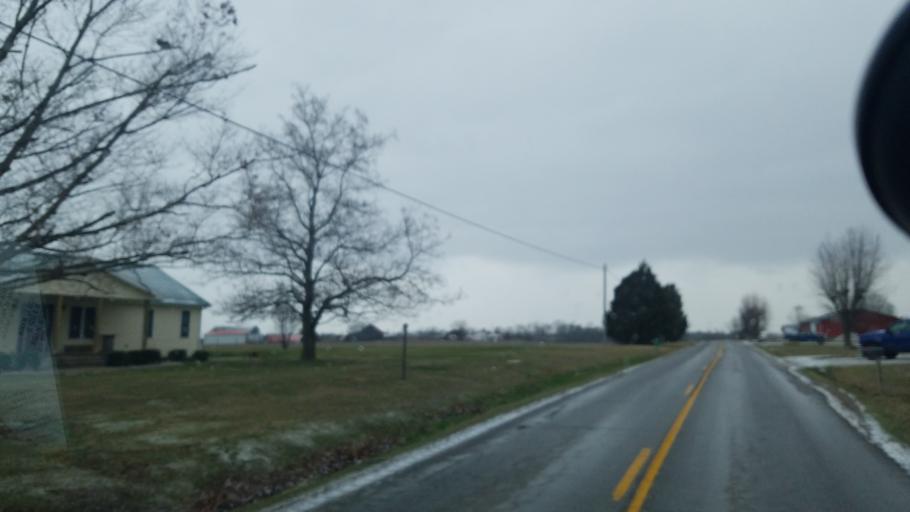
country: US
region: Kentucky
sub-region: Fleming County
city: Flemingsburg
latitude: 38.4832
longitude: -83.6099
